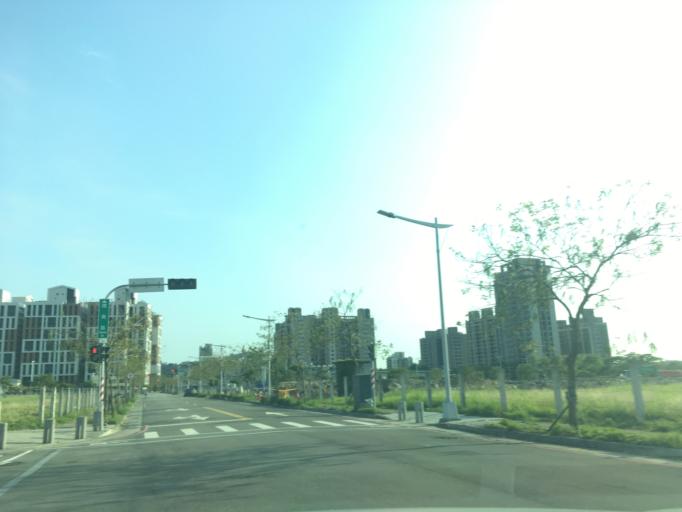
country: TW
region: Taiwan
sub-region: Taichung City
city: Taichung
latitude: 24.1994
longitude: 120.6887
